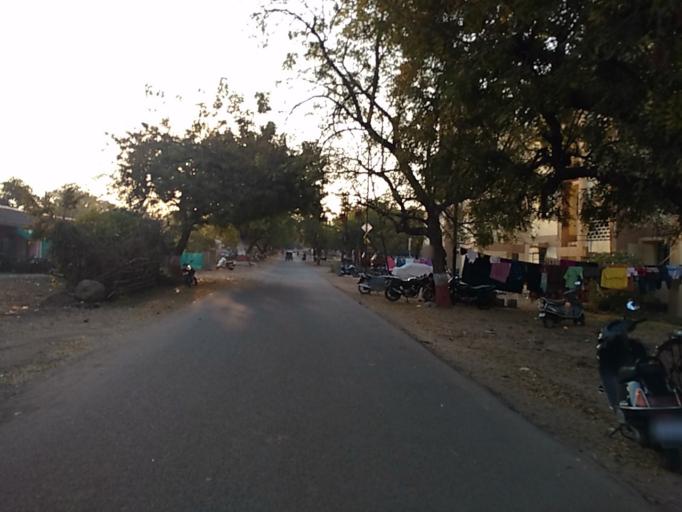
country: IN
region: Maharashtra
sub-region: Nagpur Division
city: Nagpur
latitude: 21.1791
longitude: 79.0669
